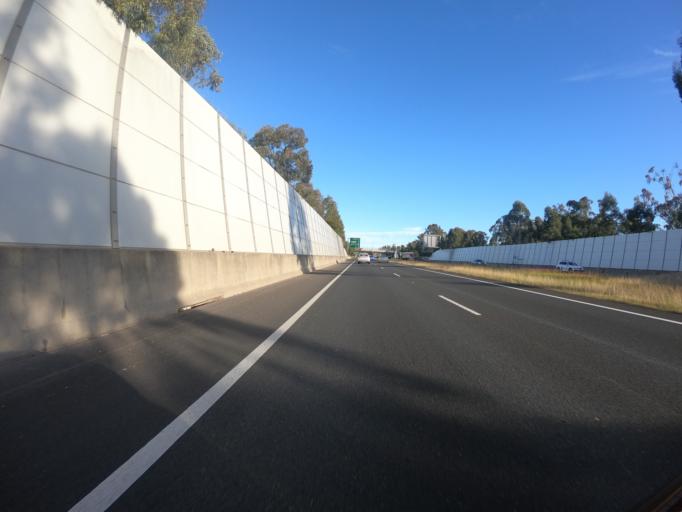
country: AU
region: New South Wales
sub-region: Blacktown
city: Glendenning
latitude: -33.7428
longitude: 150.8472
